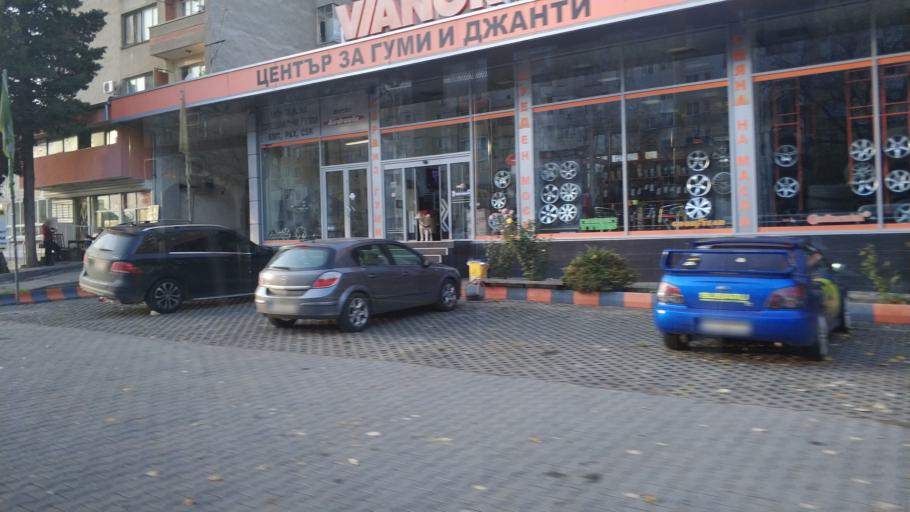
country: BG
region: Stara Zagora
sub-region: Obshtina Stara Zagora
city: Stara Zagora
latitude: 42.4187
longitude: 25.6220
